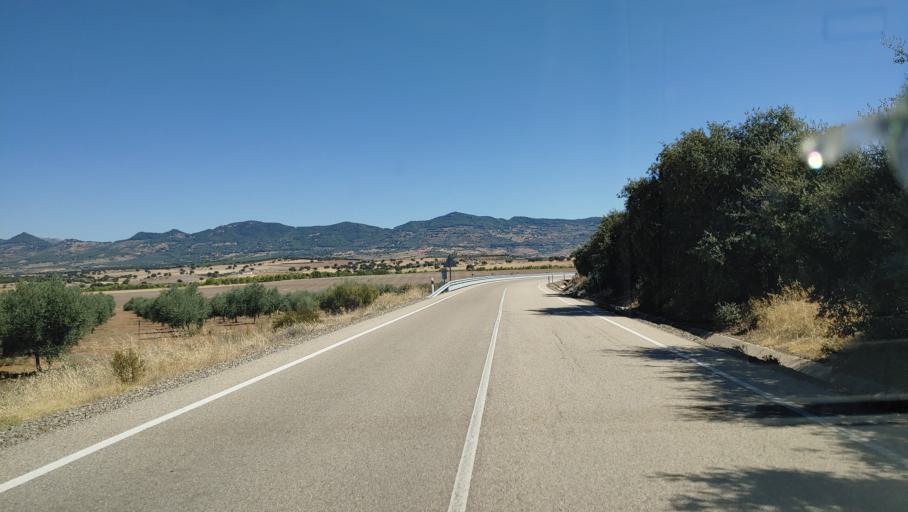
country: ES
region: Andalusia
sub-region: Provincia de Jaen
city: Genave
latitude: 38.4800
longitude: -2.7624
